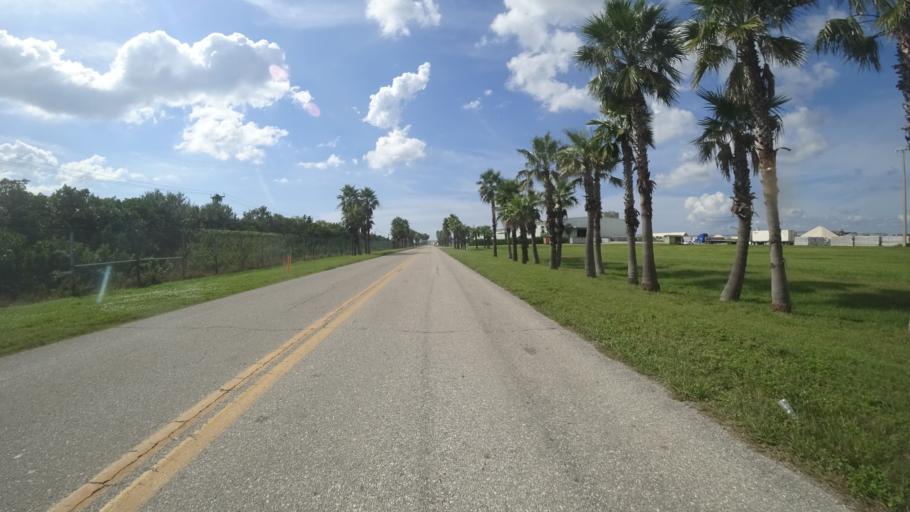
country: US
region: Florida
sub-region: Manatee County
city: Memphis
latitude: 27.6311
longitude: -82.5505
